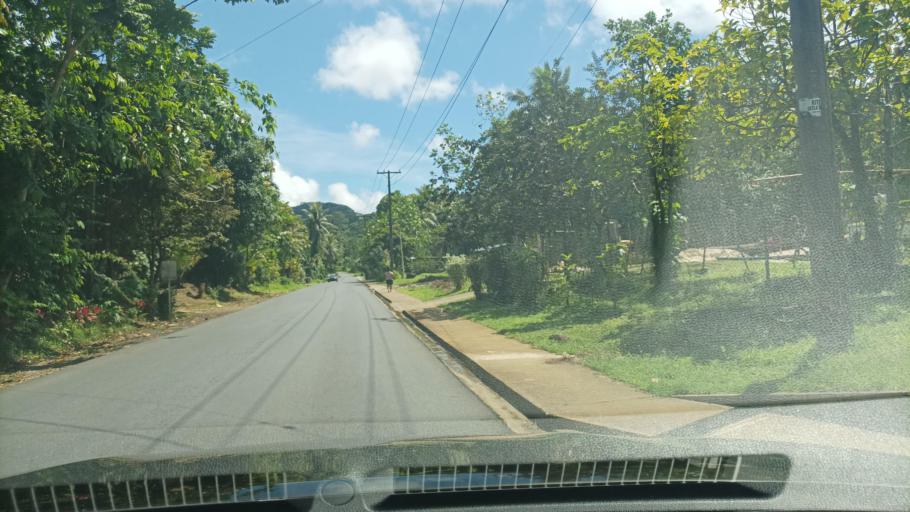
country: FM
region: Pohnpei
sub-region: Sokehs Municipality
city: Palikir - National Government Center
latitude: 6.9364
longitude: 158.1834
